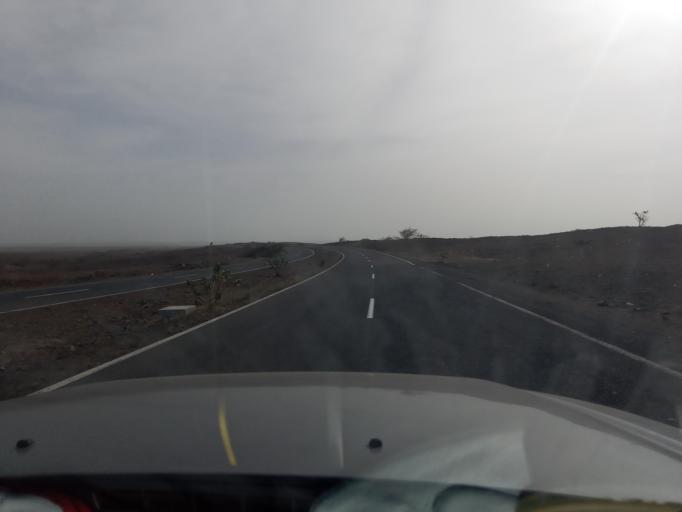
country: CV
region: Sal
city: Espargos
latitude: 16.7220
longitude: -22.9394
